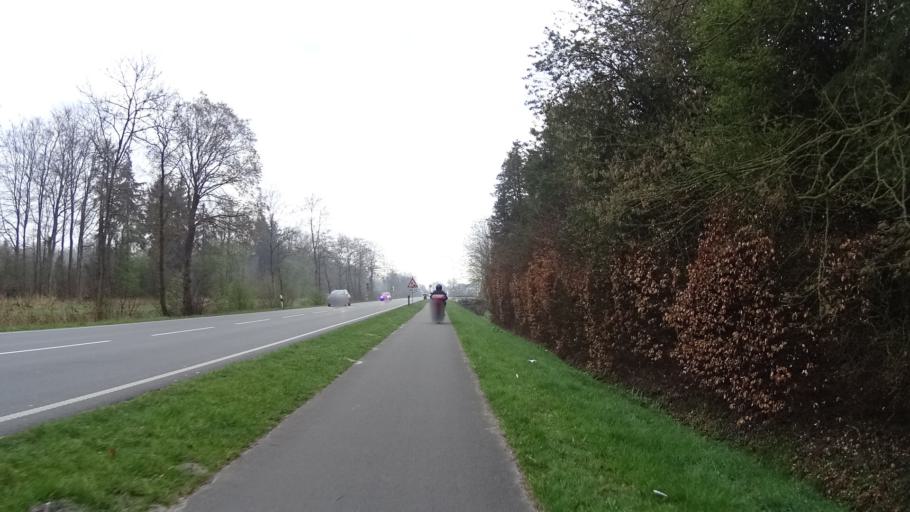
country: DE
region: Lower Saxony
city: Lutetsburg
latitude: 53.5699
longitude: 7.2413
